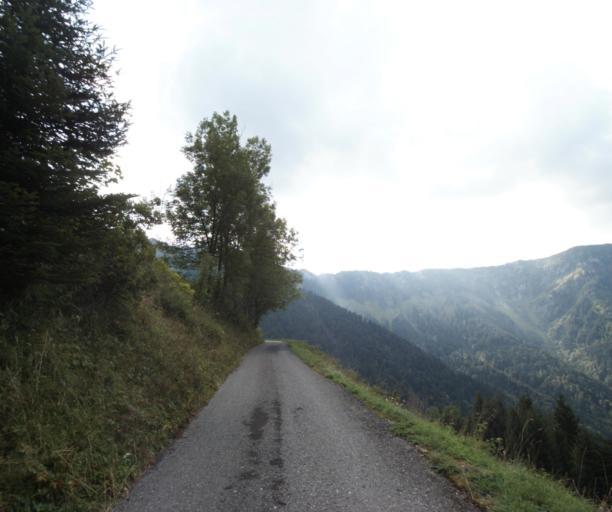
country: CH
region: Vaud
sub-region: Riviera-Pays-d'Enhaut District
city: Caux
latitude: 46.4201
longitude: 6.9721
